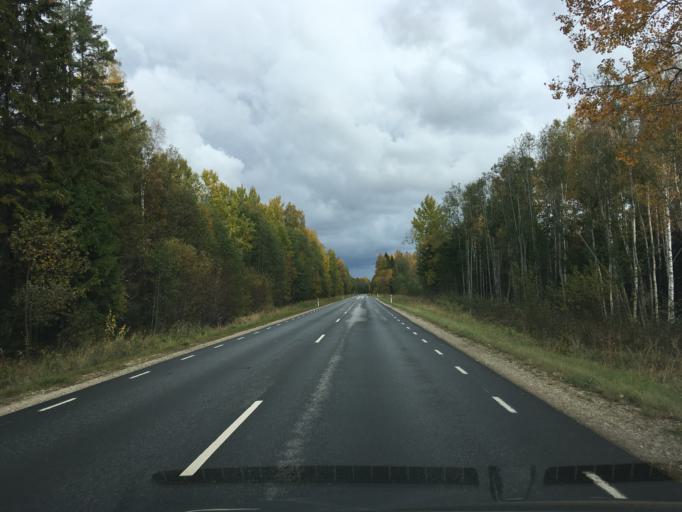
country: EE
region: Harju
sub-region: Anija vald
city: Kehra
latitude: 59.2661
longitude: 25.3539
